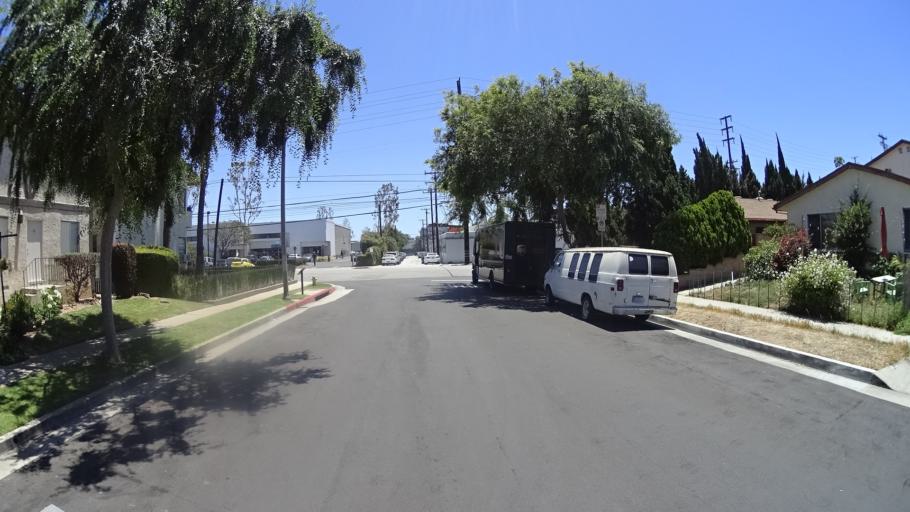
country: US
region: California
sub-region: Los Angeles County
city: Santa Monica
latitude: 34.0328
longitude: -118.4626
